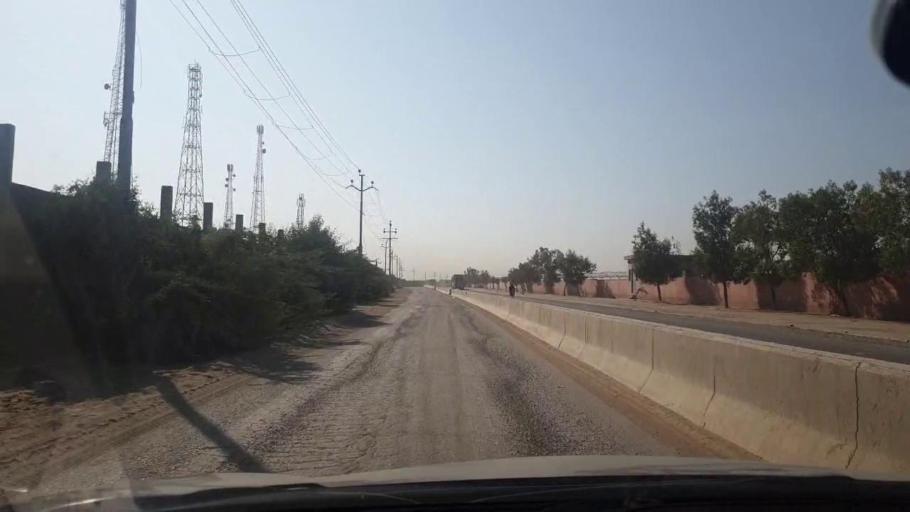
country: PK
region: Sindh
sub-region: Karachi District
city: Karachi
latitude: 25.0805
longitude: 67.0132
